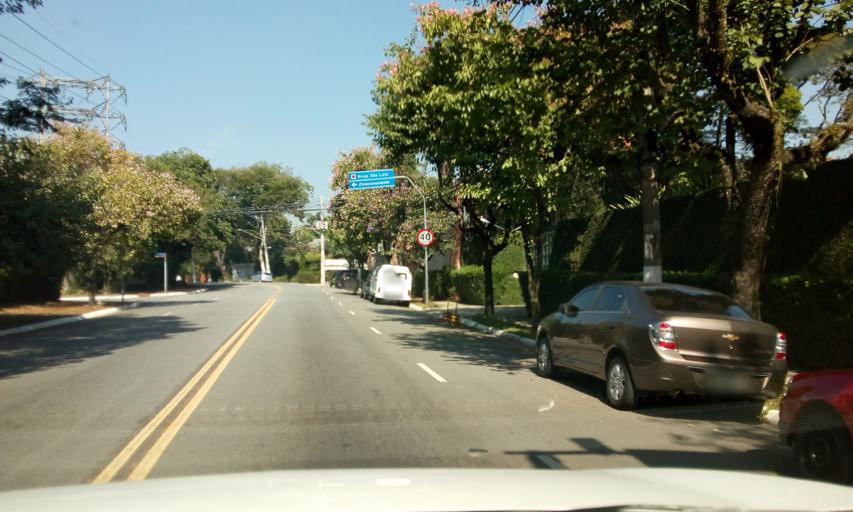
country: BR
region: Sao Paulo
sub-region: Sao Paulo
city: Sao Paulo
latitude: -23.5890
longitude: -46.7060
